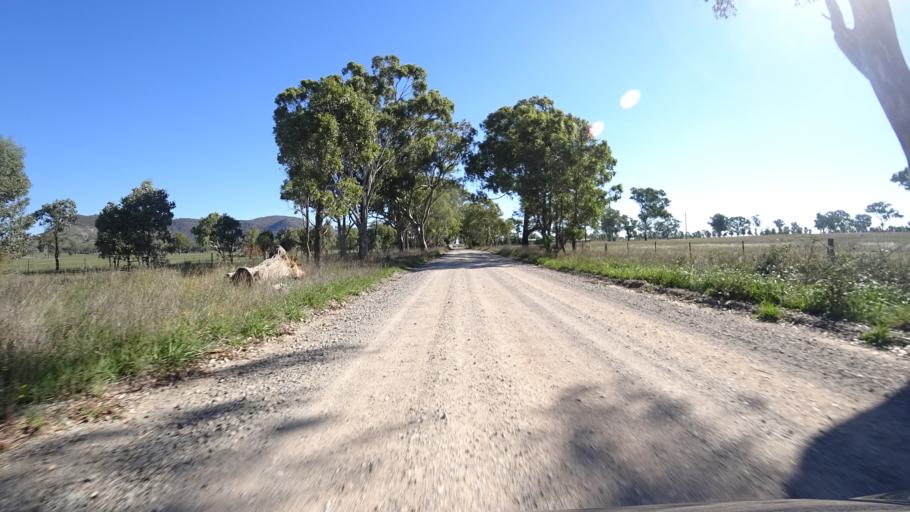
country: AU
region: New South Wales
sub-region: Mid-Western Regional
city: Kandos
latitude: -32.8279
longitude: 150.0184
